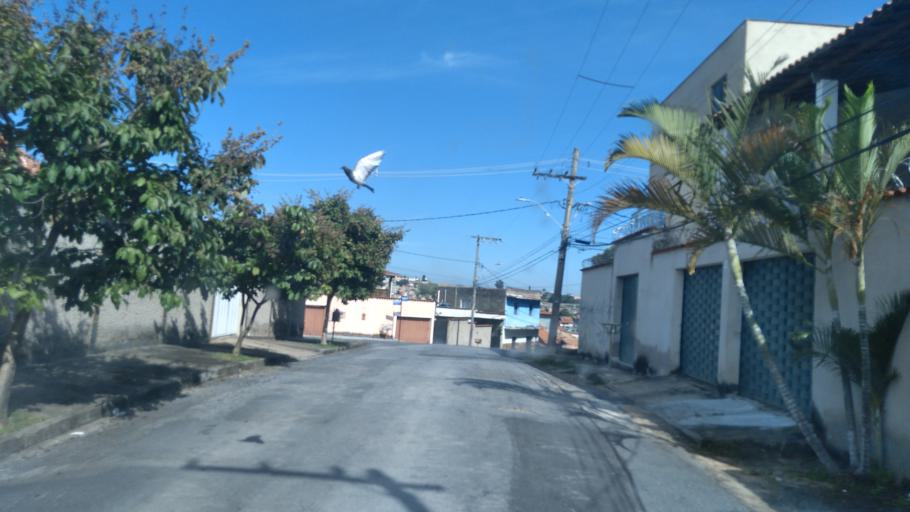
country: BR
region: Minas Gerais
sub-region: Belo Horizonte
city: Belo Horizonte
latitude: -19.8629
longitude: -43.9029
